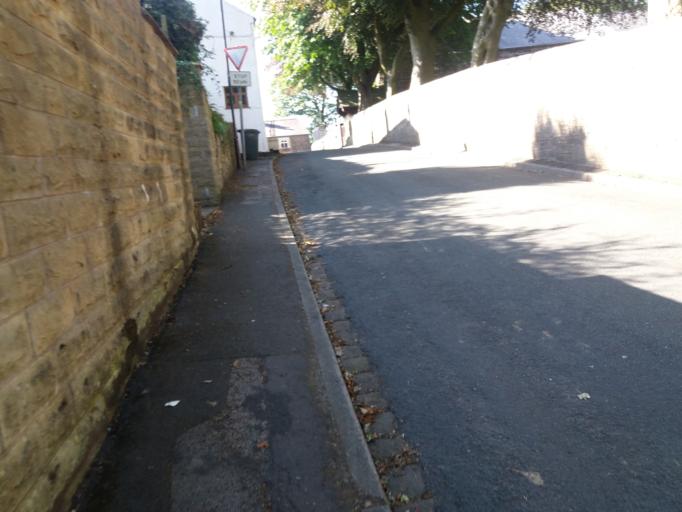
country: GB
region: England
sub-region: Lancashire
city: Clayton-le-Woods
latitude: 53.7129
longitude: -2.6087
